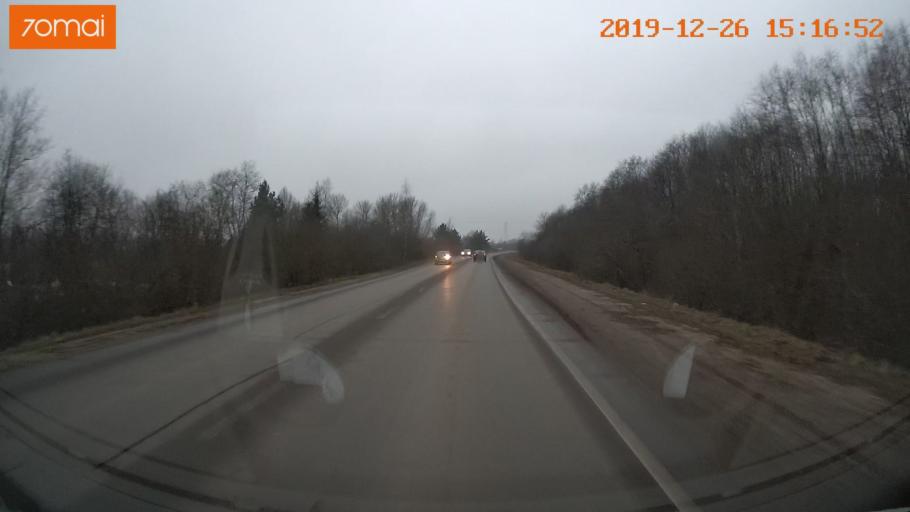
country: RU
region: Jaroslavl
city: Rybinsk
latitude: 58.0819
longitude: 38.8586
